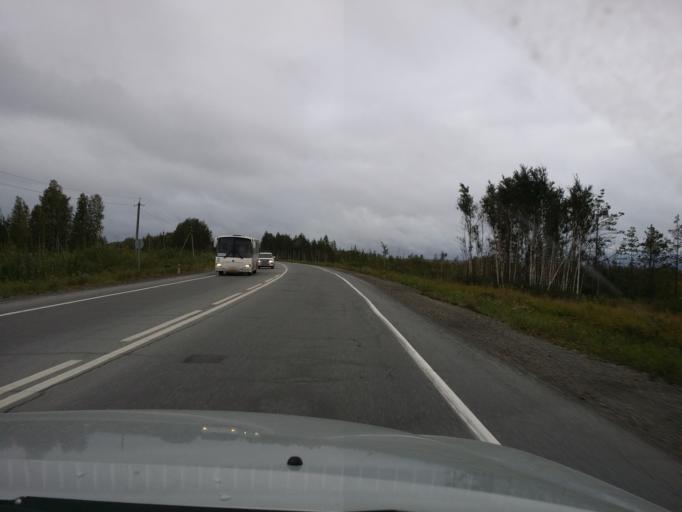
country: RU
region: Khanty-Mansiyskiy Avtonomnyy Okrug
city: Megion
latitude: 61.0688
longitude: 76.2470
